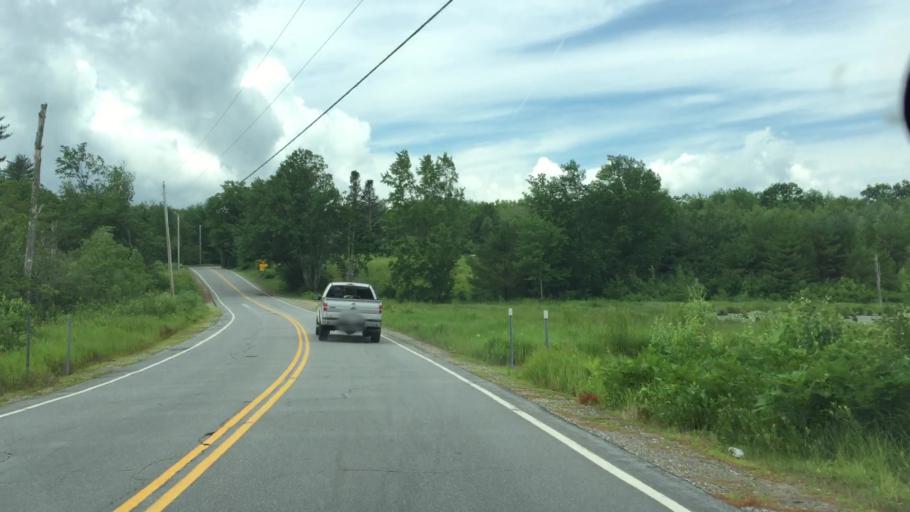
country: US
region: New Hampshire
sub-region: Carroll County
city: Sandwich
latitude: 43.8039
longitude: -71.4692
